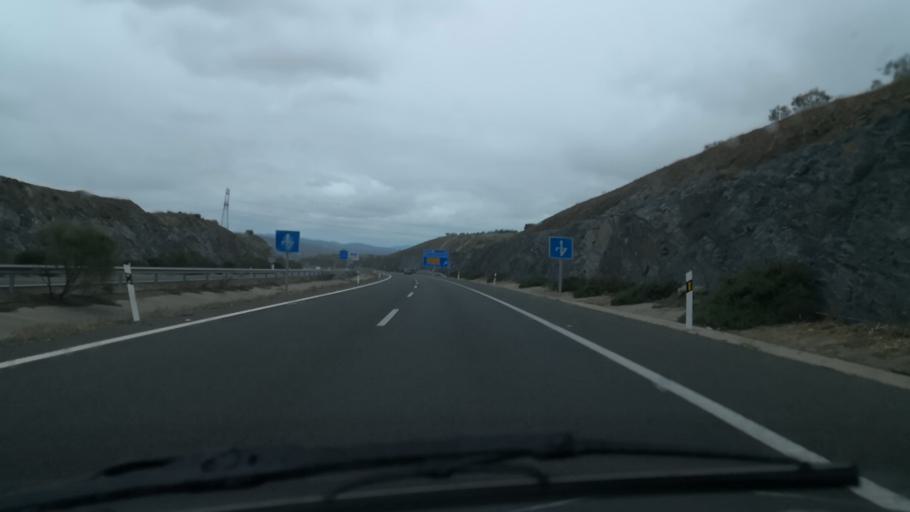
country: ES
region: Extremadura
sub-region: Provincia de Caceres
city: Plasencia
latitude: 39.9924
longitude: -6.1495
